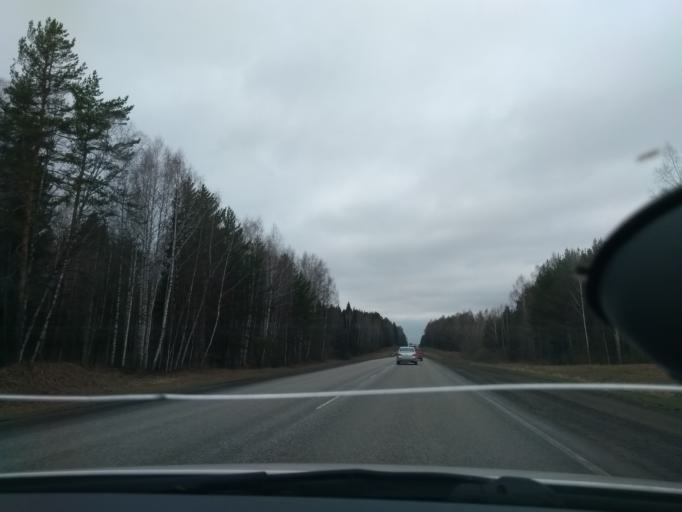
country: RU
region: Perm
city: Kungur
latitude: 57.4345
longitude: 56.8249
